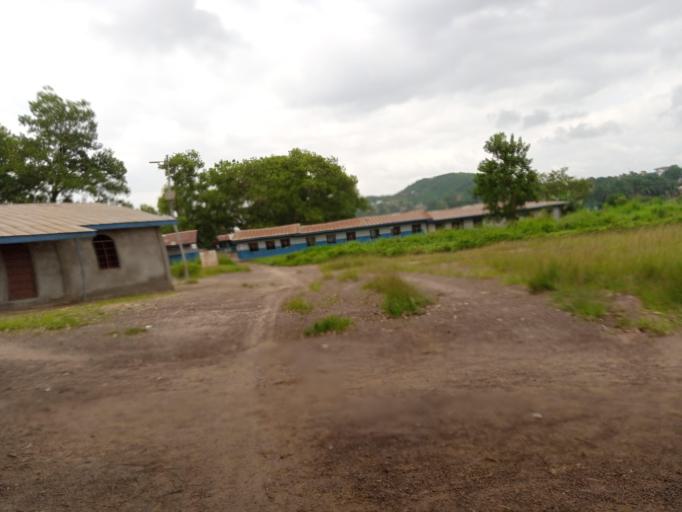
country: SL
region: Eastern Province
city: Kenema
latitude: 7.8612
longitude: -11.1974
